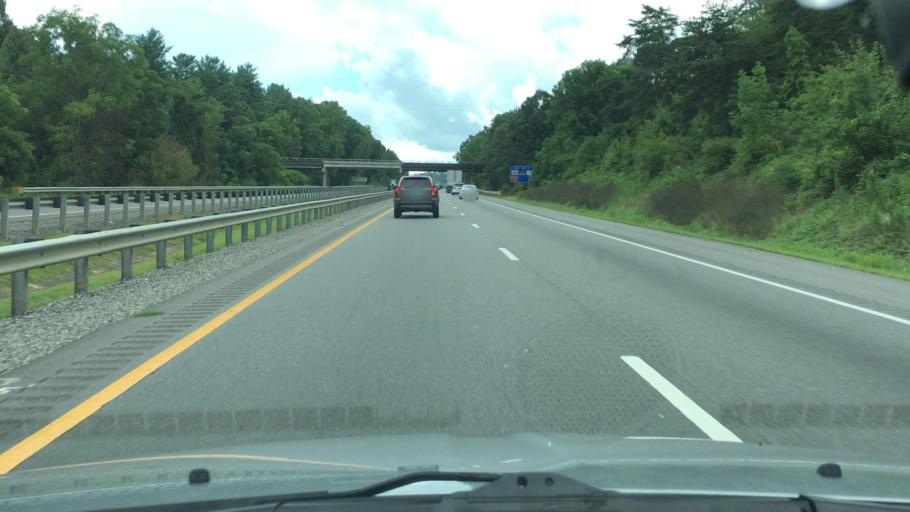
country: US
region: North Carolina
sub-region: Buncombe County
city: Weaverville
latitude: 35.6858
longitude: -82.5802
